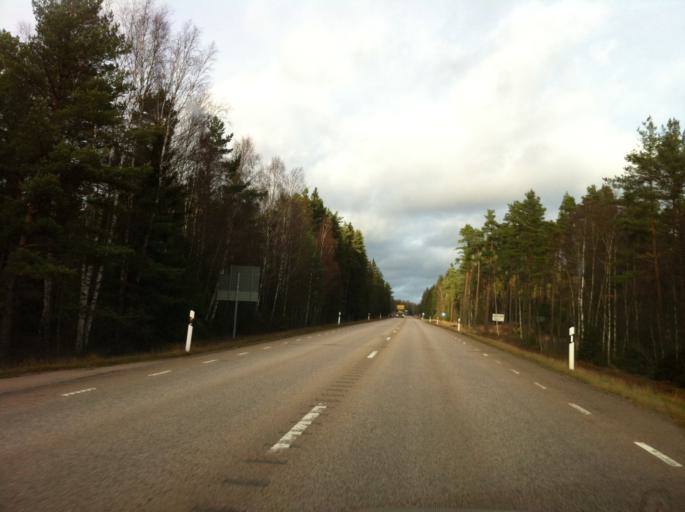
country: SE
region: Kronoberg
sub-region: Uppvidinge Kommun
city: Lenhovda
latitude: 57.0882
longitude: 15.1847
